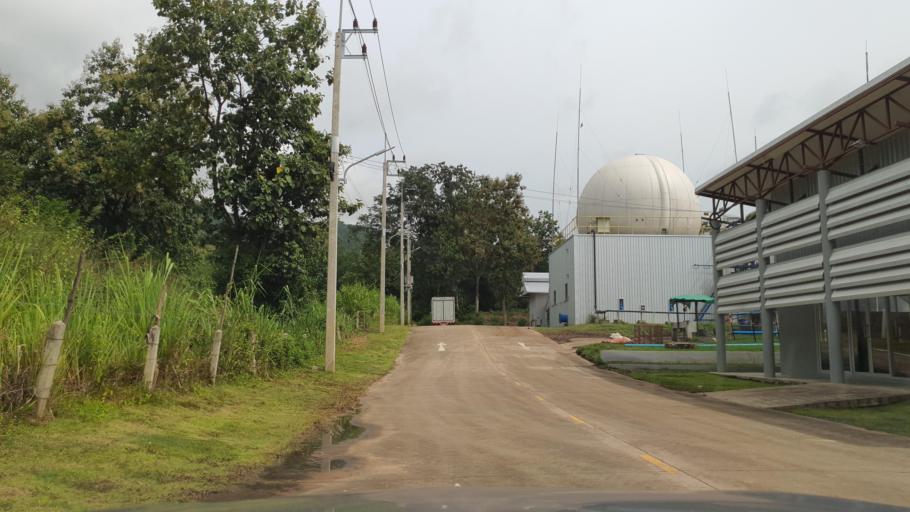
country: TH
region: Chiang Mai
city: Chiang Mai
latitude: 18.7684
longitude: 98.9366
